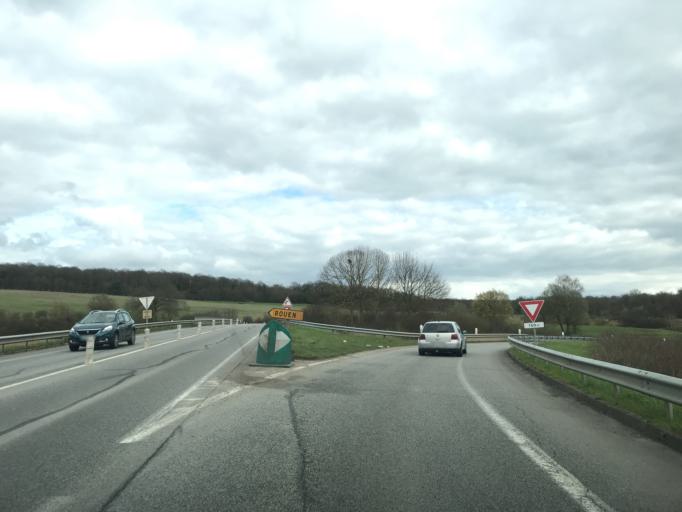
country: FR
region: Haute-Normandie
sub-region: Departement de l'Eure
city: Gravigny
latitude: 49.0597
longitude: 1.1731
